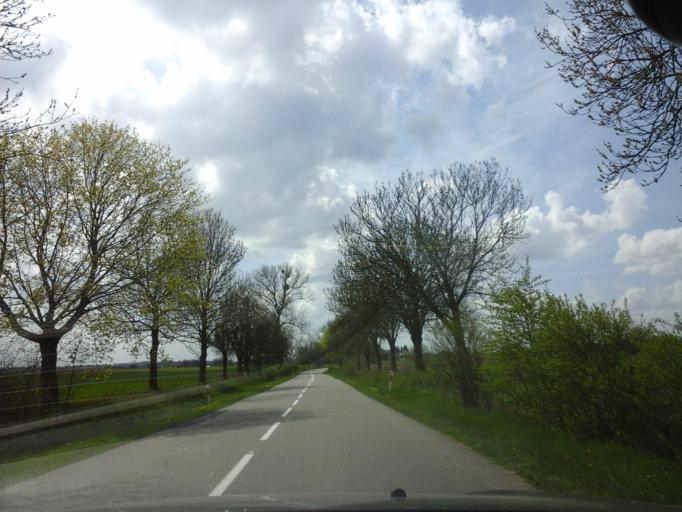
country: PL
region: West Pomeranian Voivodeship
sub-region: Powiat stargardzki
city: Suchan
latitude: 53.2937
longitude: 15.3581
